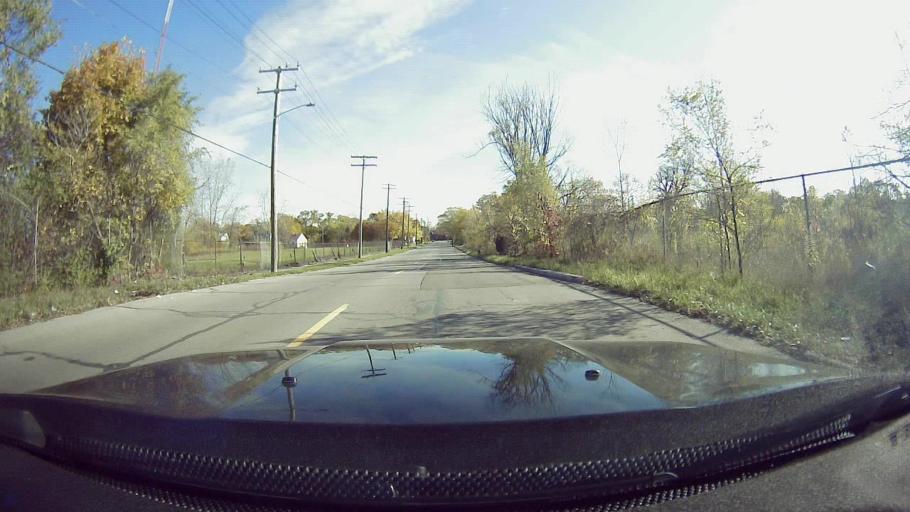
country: US
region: Michigan
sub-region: Wayne County
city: Highland Park
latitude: 42.3887
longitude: -83.1503
